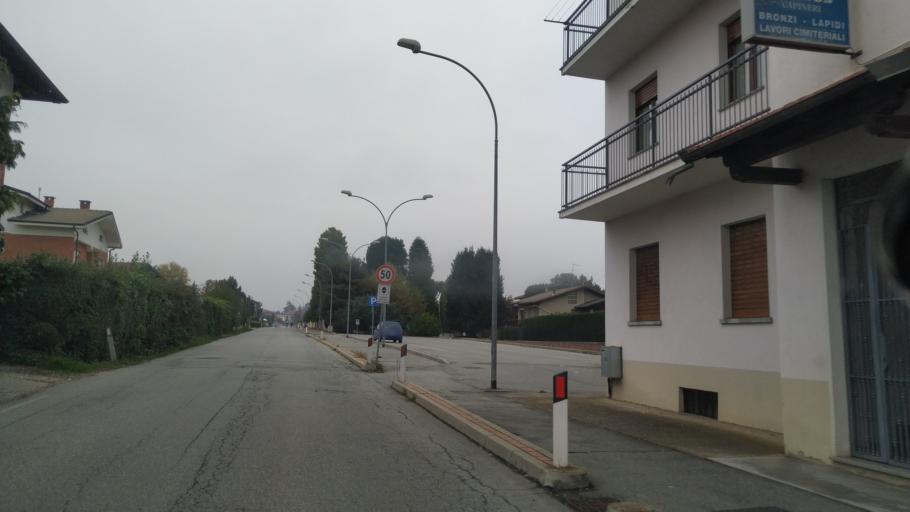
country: IT
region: Piedmont
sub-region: Provincia di Biella
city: Lessona
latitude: 45.5774
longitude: 8.2027
